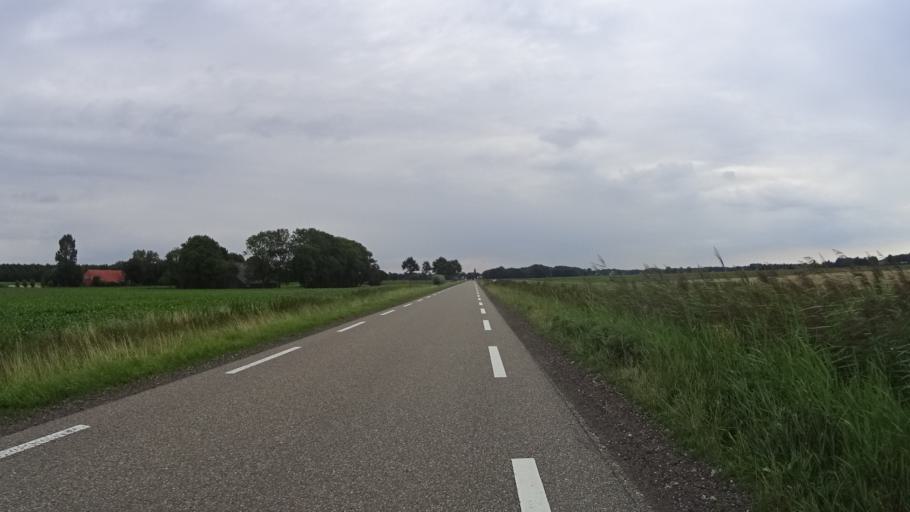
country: NL
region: Groningen
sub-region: Gemeente Slochteren
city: Slochteren
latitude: 53.2269
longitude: 6.7781
